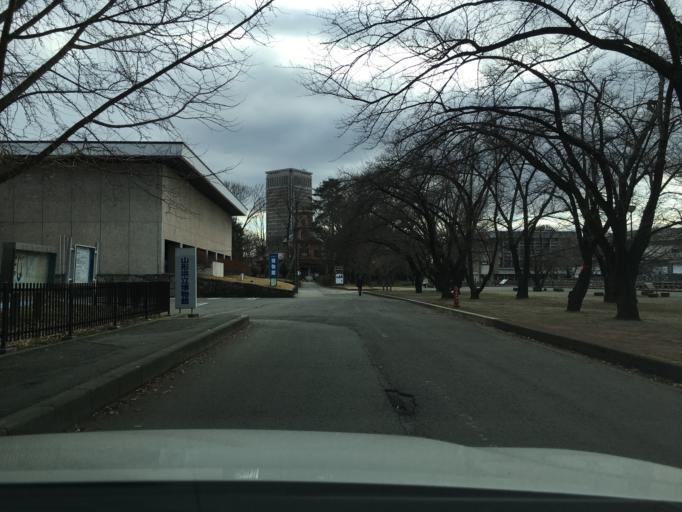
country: JP
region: Yamagata
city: Yamagata-shi
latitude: 38.2550
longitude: 140.3295
